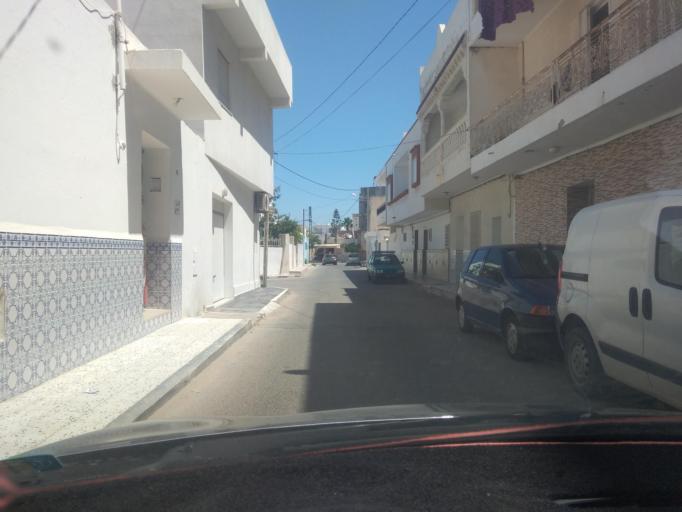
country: TN
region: Susah
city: Hammam Sousse
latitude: 35.8513
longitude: 10.5913
